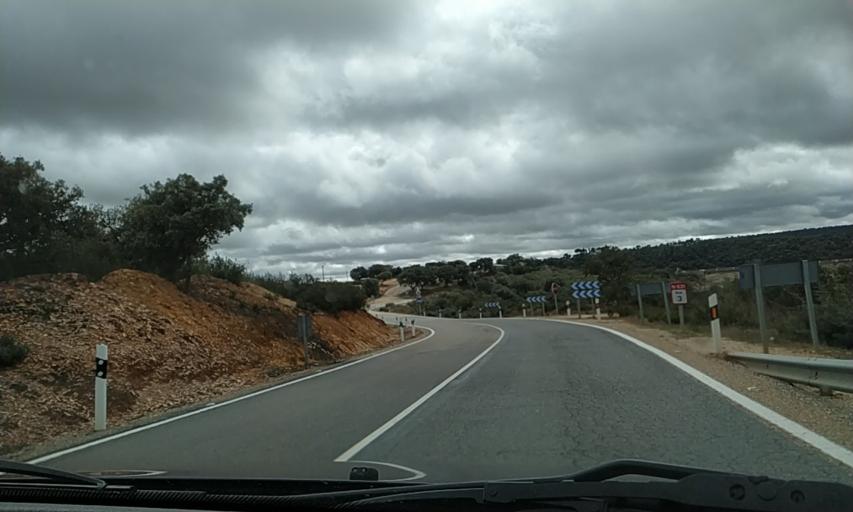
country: ES
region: Castille and Leon
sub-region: Provincia de Zamora
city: San Cebrian de Castro
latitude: 41.7059
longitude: -5.8080
